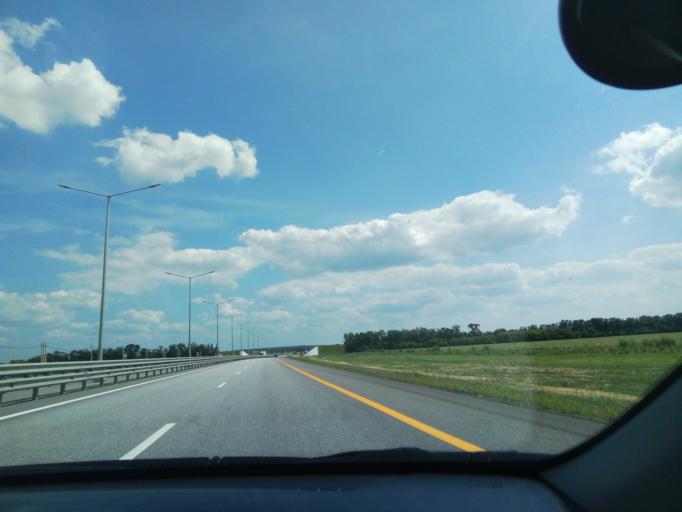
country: RU
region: Voronezj
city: Podkletnoye
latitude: 51.5379
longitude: 39.5039
